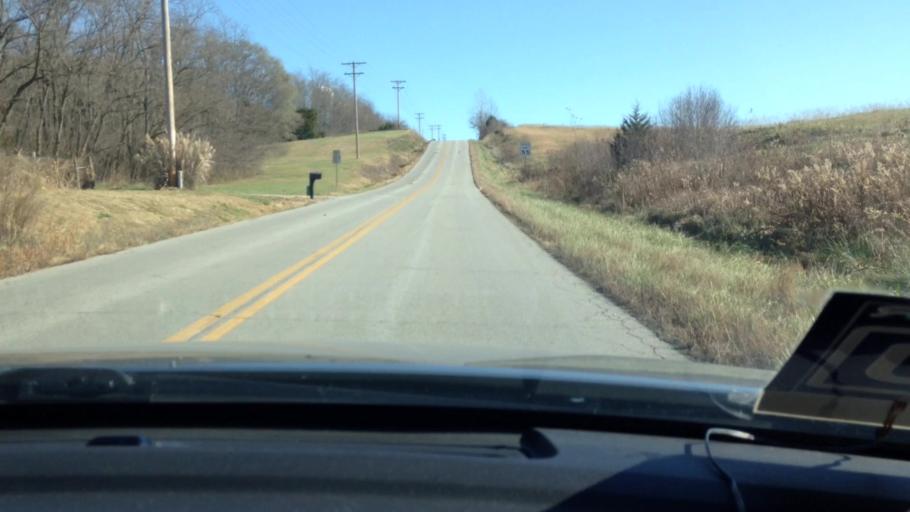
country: US
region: Missouri
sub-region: Platte County
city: Weston
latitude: 39.4828
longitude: -94.8983
